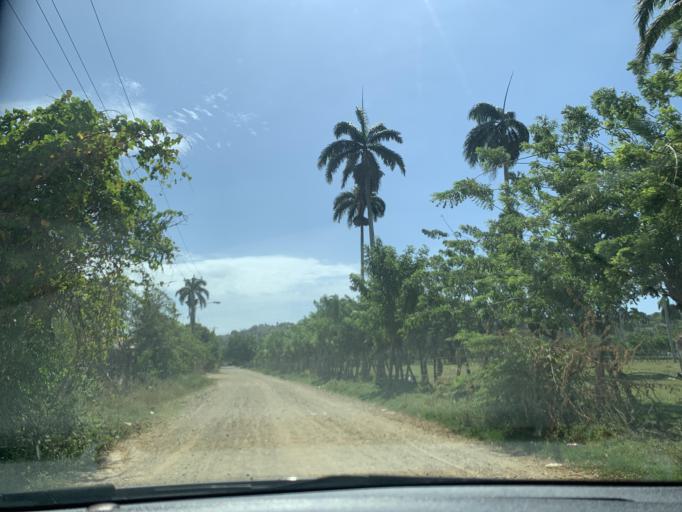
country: DO
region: Puerto Plata
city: Luperon
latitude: 19.8901
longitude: -70.8816
